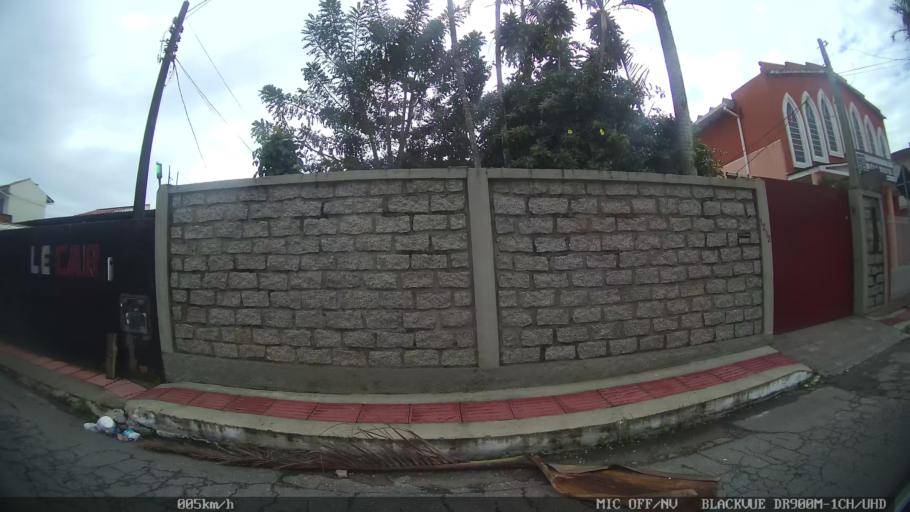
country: BR
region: Santa Catarina
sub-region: Sao Jose
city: Campinas
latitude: -27.5761
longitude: -48.6181
